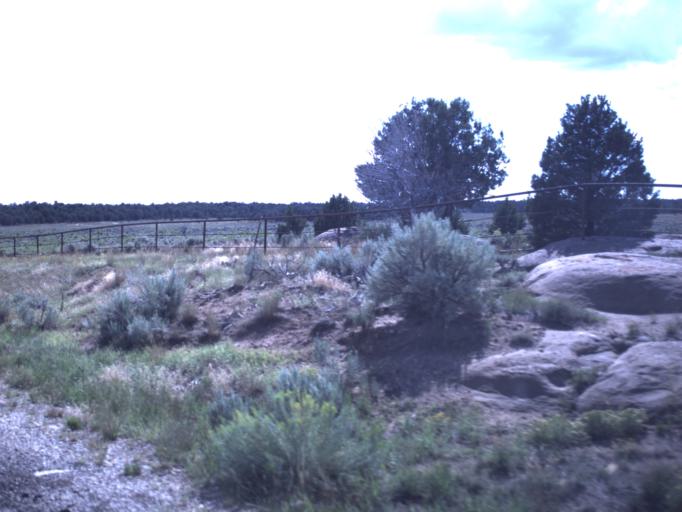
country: US
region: Utah
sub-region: Duchesne County
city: Duchesne
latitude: 40.2703
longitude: -110.7038
